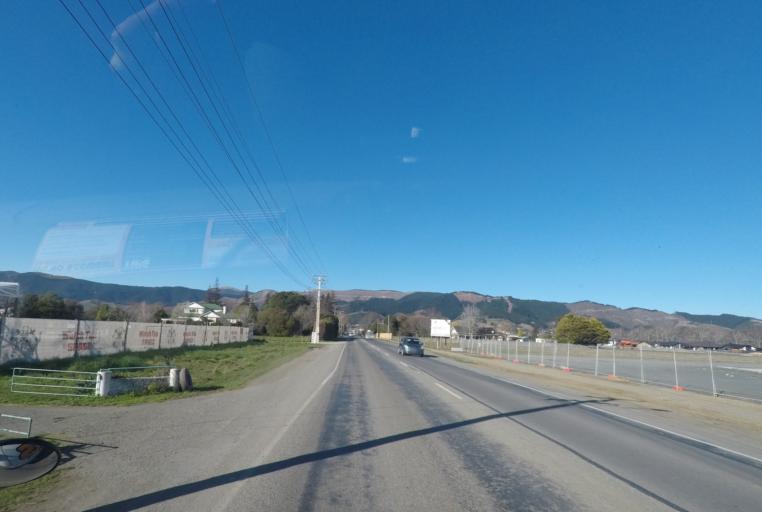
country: NZ
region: Tasman
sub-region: Tasman District
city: Richmond
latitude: -41.3304
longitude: 173.1750
